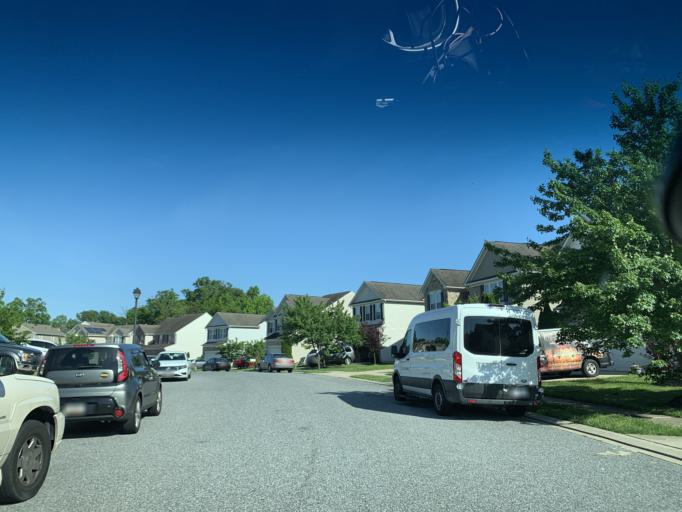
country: US
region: Maryland
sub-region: Harford County
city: Riverside
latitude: 39.4810
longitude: -76.2392
